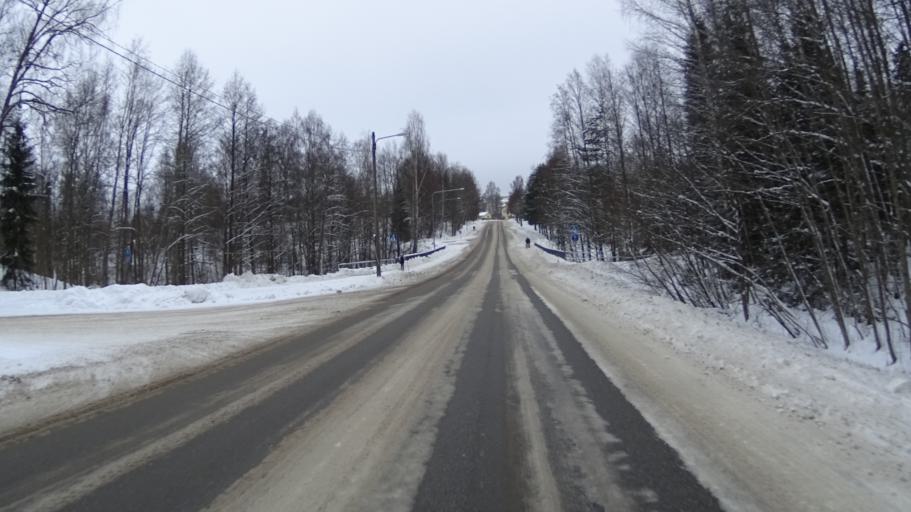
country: FI
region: Uusimaa
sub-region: Helsinki
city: Karkkila
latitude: 60.5299
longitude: 24.2072
